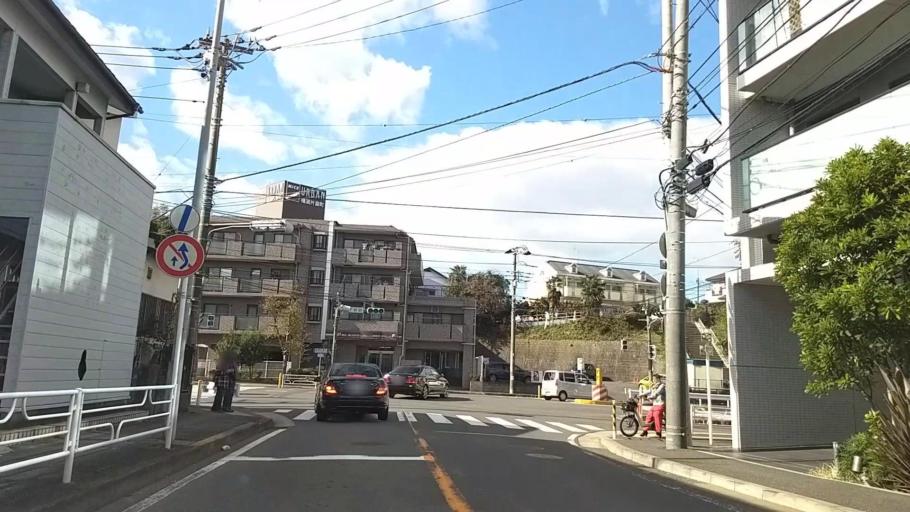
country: JP
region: Kanagawa
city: Yokohama
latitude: 35.4918
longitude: 139.6077
